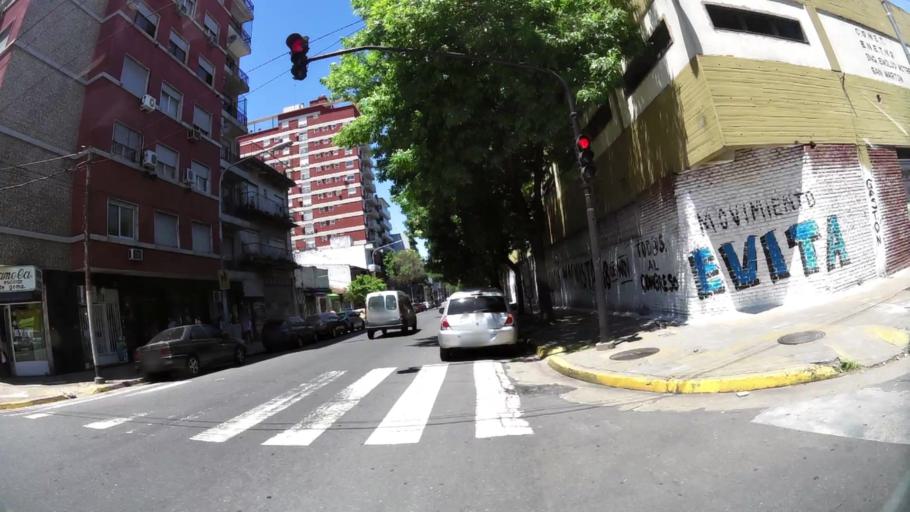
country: AR
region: Buenos Aires
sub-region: Partido de General San Martin
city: General San Martin
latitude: -34.5797
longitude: -58.5356
